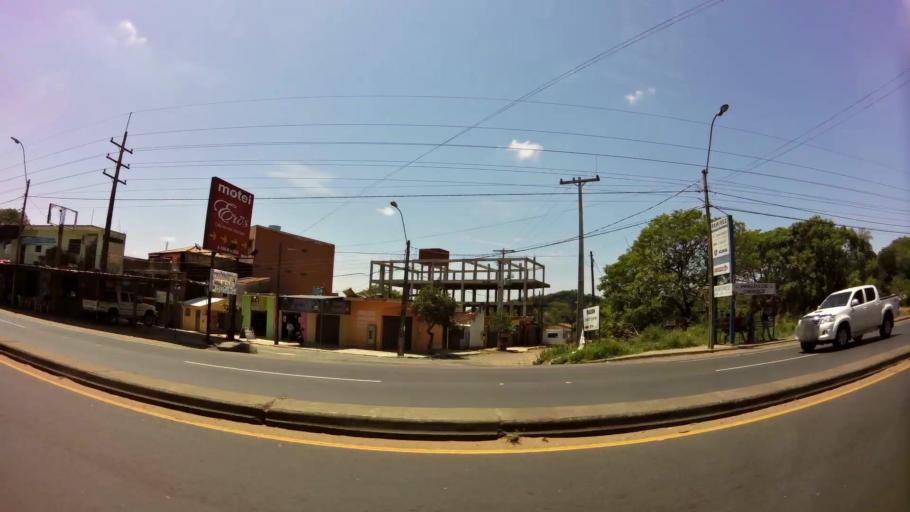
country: PY
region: Central
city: Nemby
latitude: -25.4031
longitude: -57.5431
